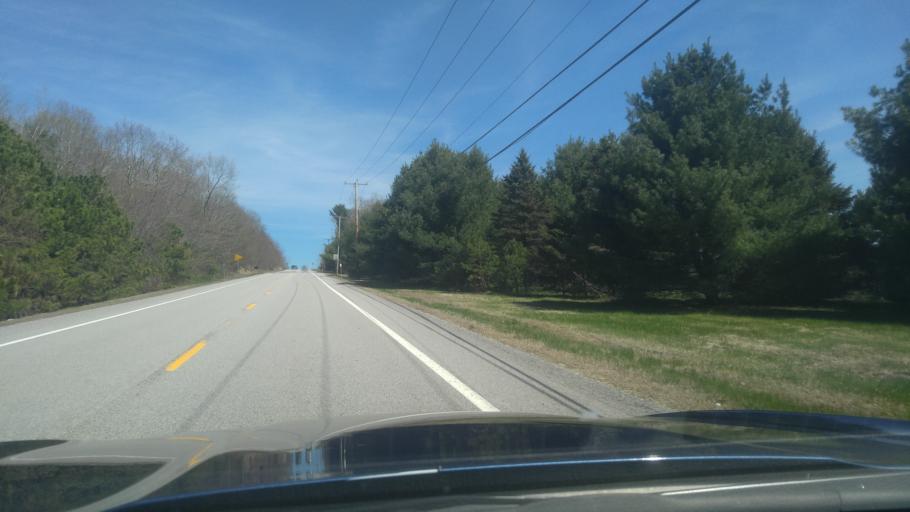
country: US
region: Rhode Island
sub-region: Washington County
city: Hope Valley
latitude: 41.5752
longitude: -71.7427
